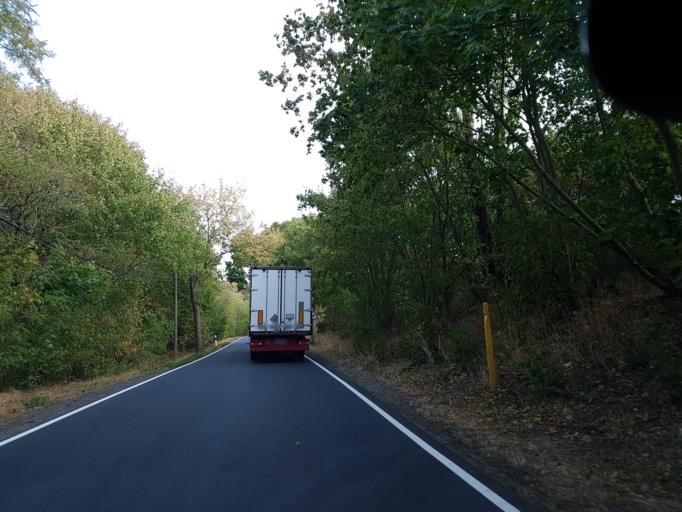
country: DE
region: Saxony-Anhalt
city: Pretzsch
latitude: 51.7083
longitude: 12.8076
